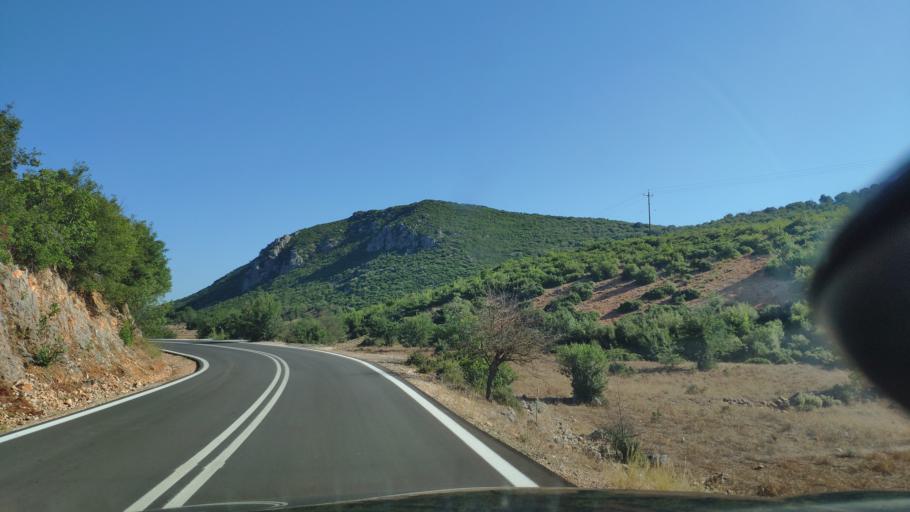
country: GR
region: West Greece
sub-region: Nomos Aitolias kai Akarnanias
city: Fitiai
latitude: 38.6705
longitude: 21.1406
